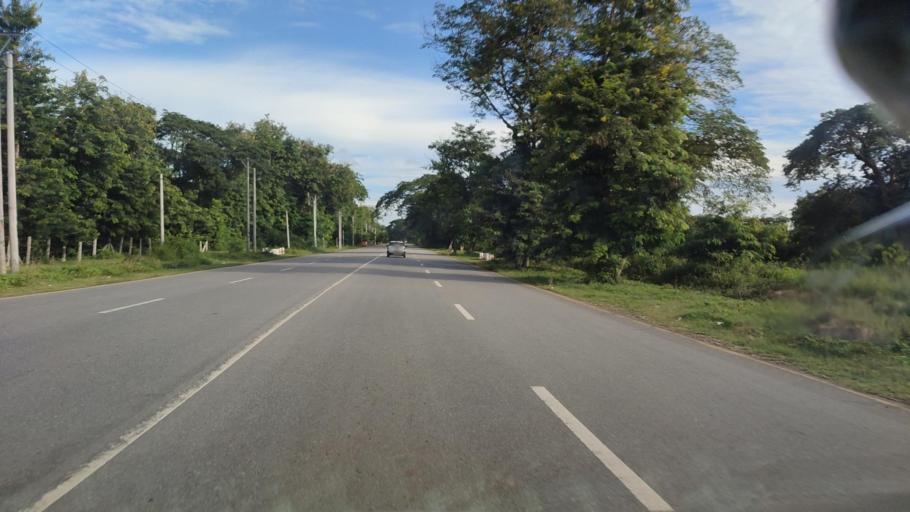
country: MM
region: Mandalay
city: Yamethin
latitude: 20.1910
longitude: 96.1848
